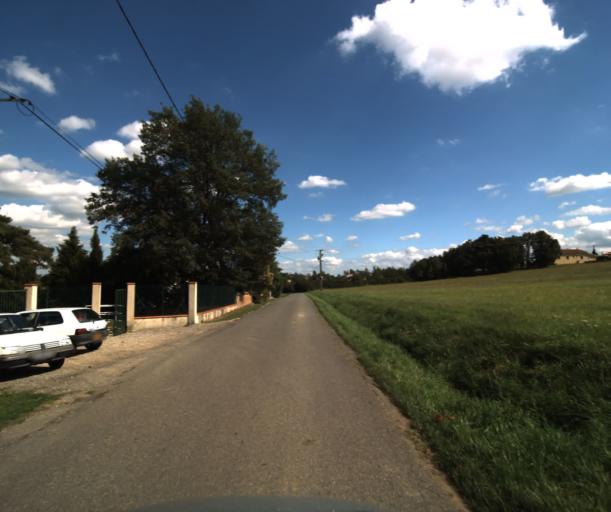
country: FR
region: Midi-Pyrenees
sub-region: Departement de la Haute-Garonne
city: Eaunes
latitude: 43.4181
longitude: 1.3538
